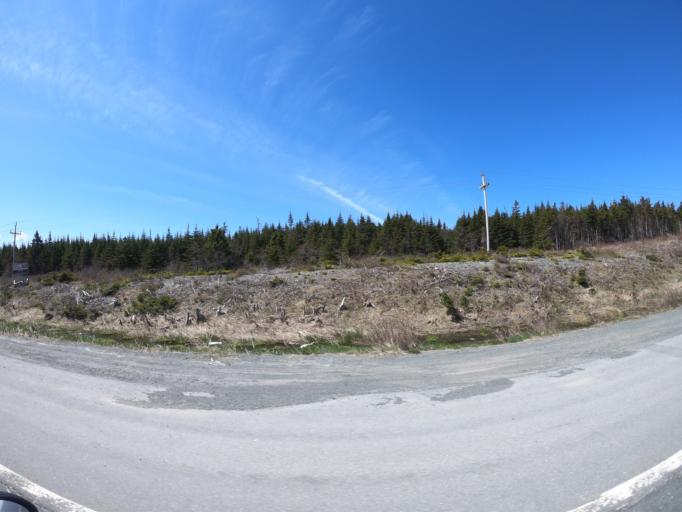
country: CA
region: Newfoundland and Labrador
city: Mount Pearl
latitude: 47.5037
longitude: -52.8200
